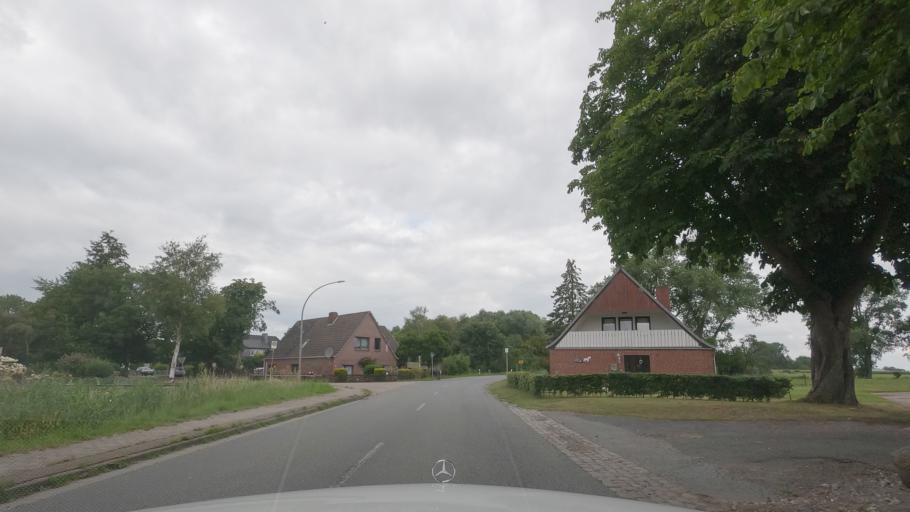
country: DE
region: Lower Saxony
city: Neuenkirchen
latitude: 53.2864
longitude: 8.5325
